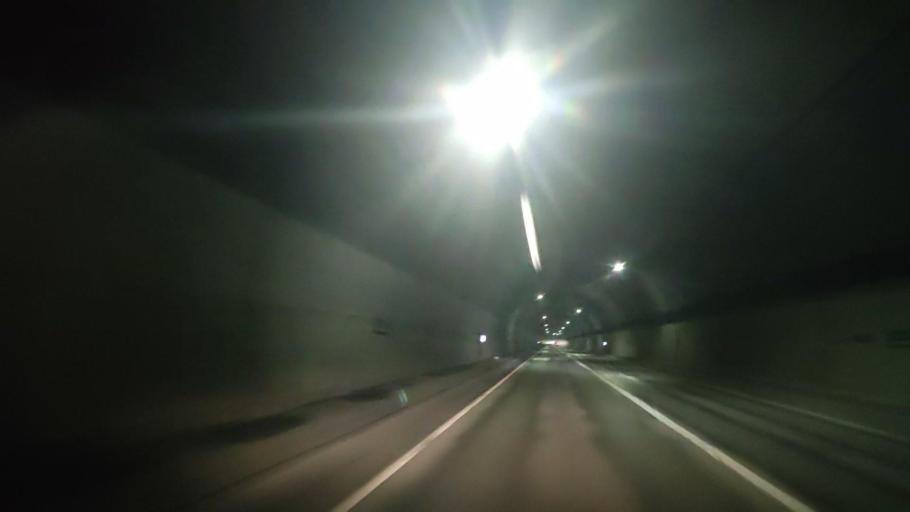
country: JP
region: Hokkaido
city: Niseko Town
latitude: 42.5970
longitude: 140.5473
